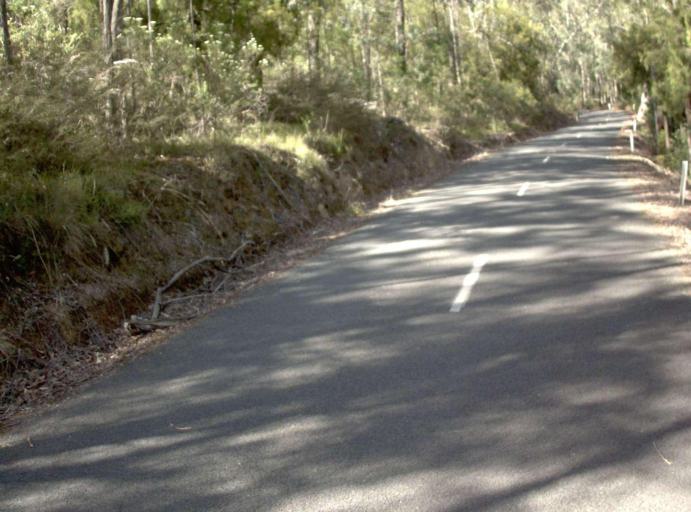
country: AU
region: Victoria
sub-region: East Gippsland
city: Lakes Entrance
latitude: -37.4625
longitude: 148.5660
